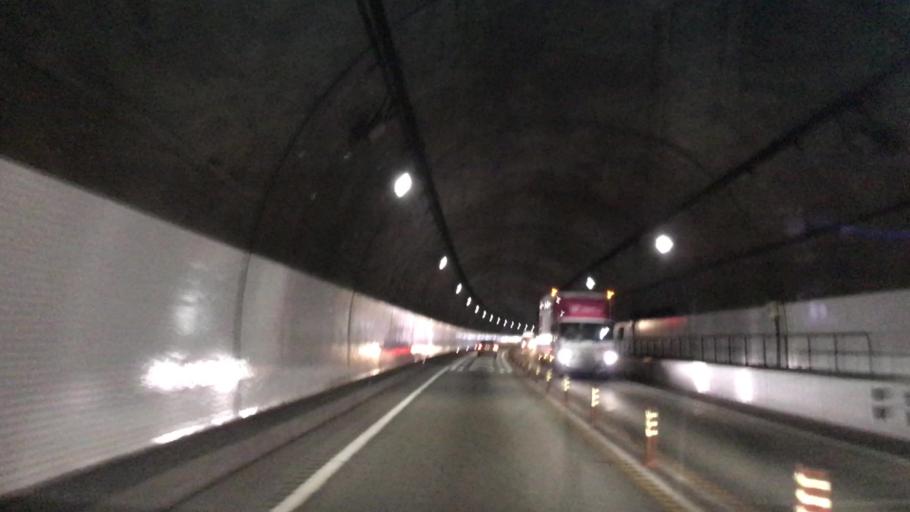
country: JP
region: Hokkaido
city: Iwamizawa
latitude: 42.9351
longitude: 142.0909
